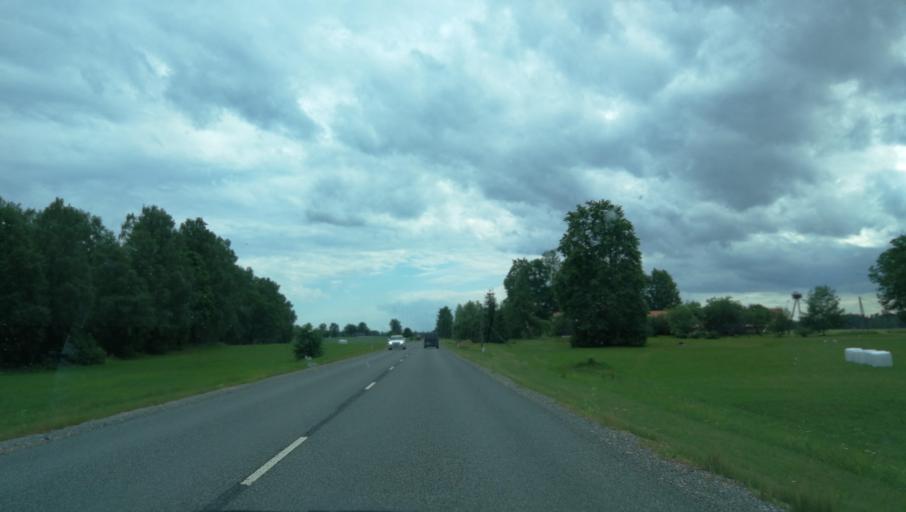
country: LV
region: Naukseni
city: Naukseni
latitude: 57.7406
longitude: 25.4289
